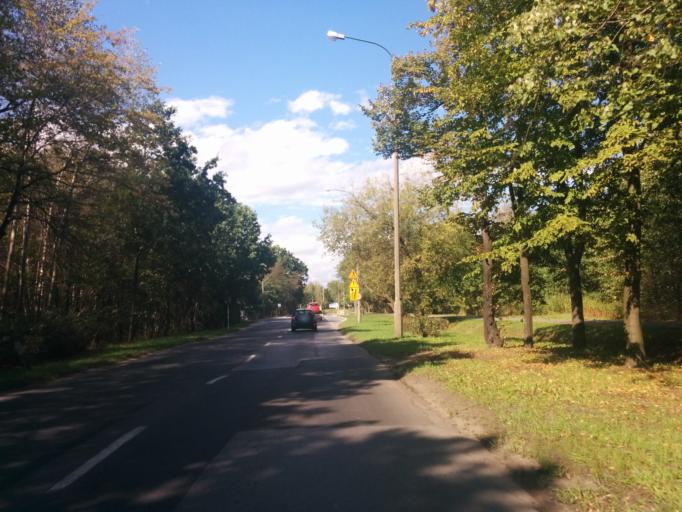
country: PL
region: Masovian Voivodeship
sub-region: Warszawa
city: Bialoleka
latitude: 52.3262
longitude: 20.9920
